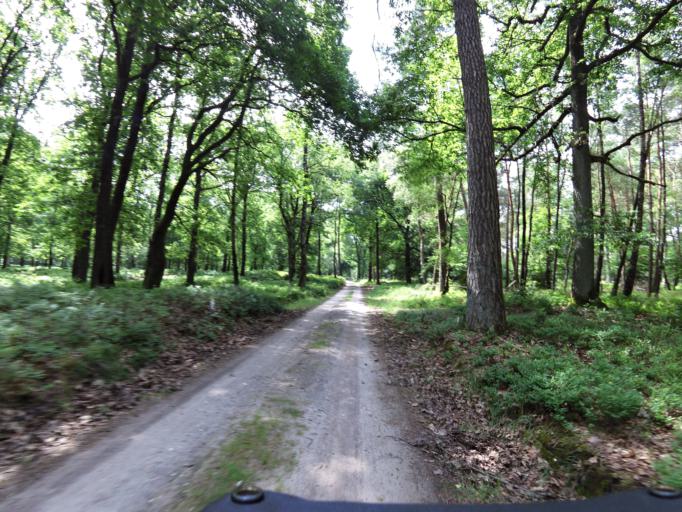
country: NL
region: Gelderland
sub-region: Gemeente Rozendaal
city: Rozendaal
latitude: 52.0672
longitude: 5.9799
